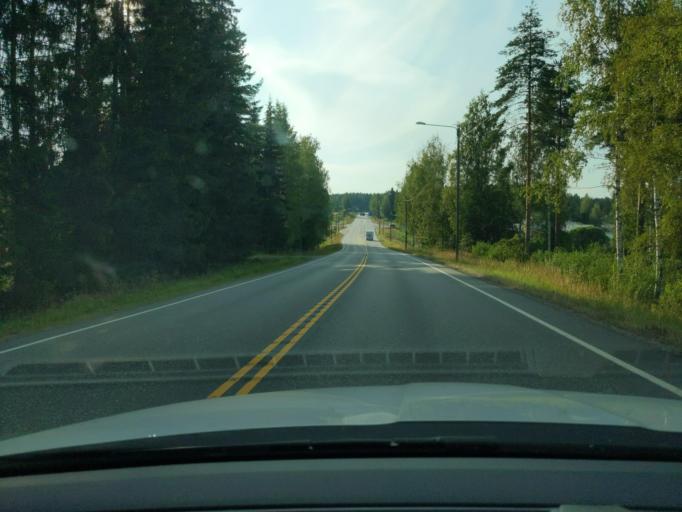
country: FI
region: Paijanne Tavastia
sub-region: Lahti
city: Padasjoki
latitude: 61.3422
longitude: 25.2525
